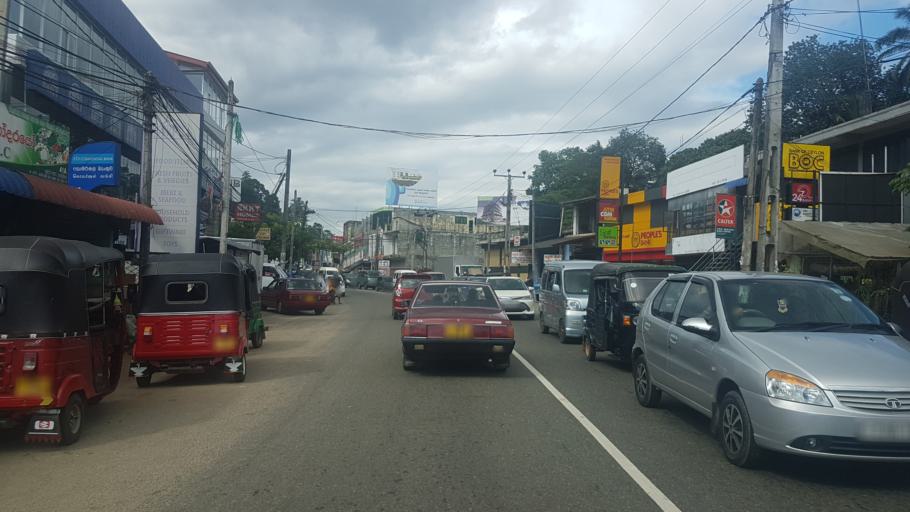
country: LK
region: Central
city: Gampola
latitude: 7.2149
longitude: 80.5980
